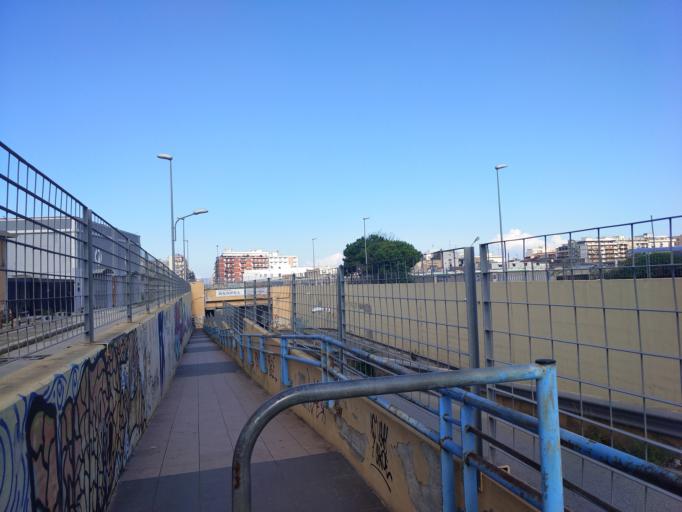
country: IT
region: Apulia
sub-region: Provincia di Bari
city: Bari
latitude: 41.1147
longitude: 16.8527
